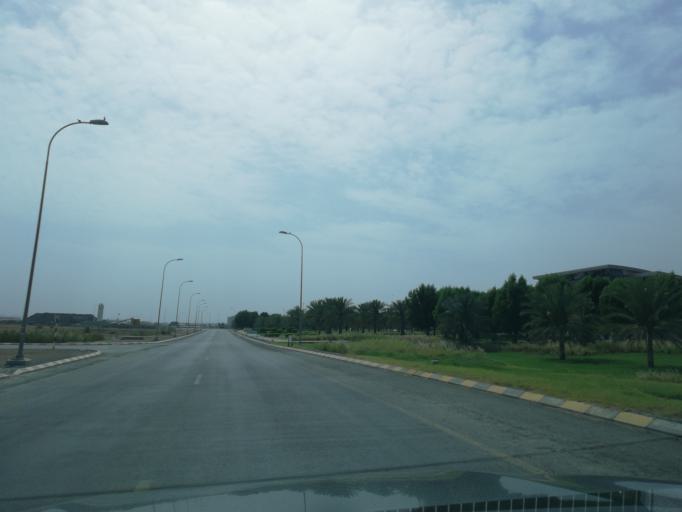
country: OM
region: Muhafazat Masqat
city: As Sib al Jadidah
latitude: 23.6194
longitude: 58.2669
